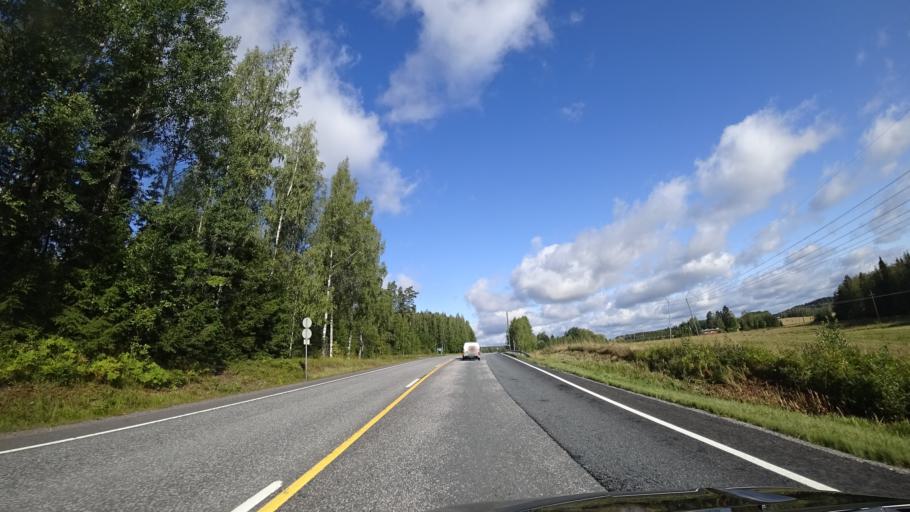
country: FI
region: Uusimaa
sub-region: Helsinki
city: Tuusula
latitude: 60.4584
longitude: 24.9496
